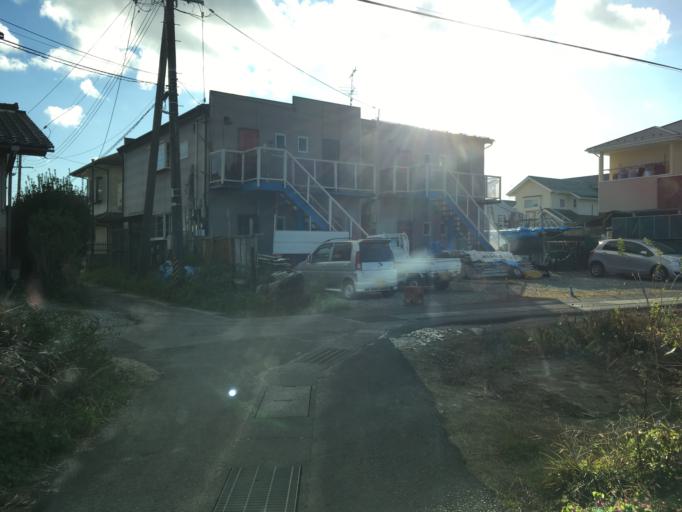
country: JP
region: Fukushima
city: Fukushima-shi
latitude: 37.7851
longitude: 140.4983
